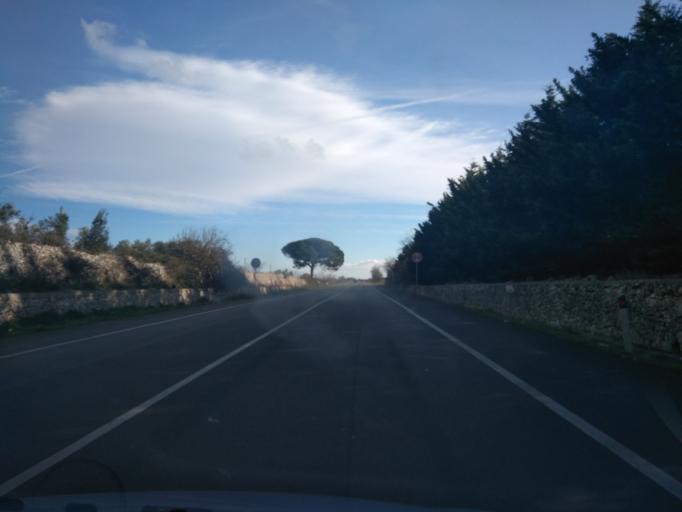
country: IT
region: Apulia
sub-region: Provincia di Bari
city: Gioia del Colle
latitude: 40.7515
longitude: 16.9637
